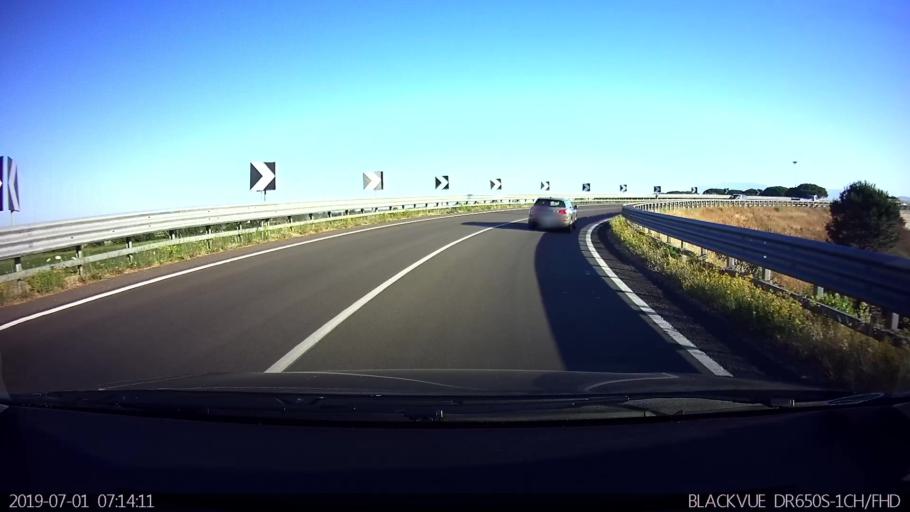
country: IT
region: Latium
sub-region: Provincia di Latina
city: Borgo Hermada
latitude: 41.3205
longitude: 13.1833
